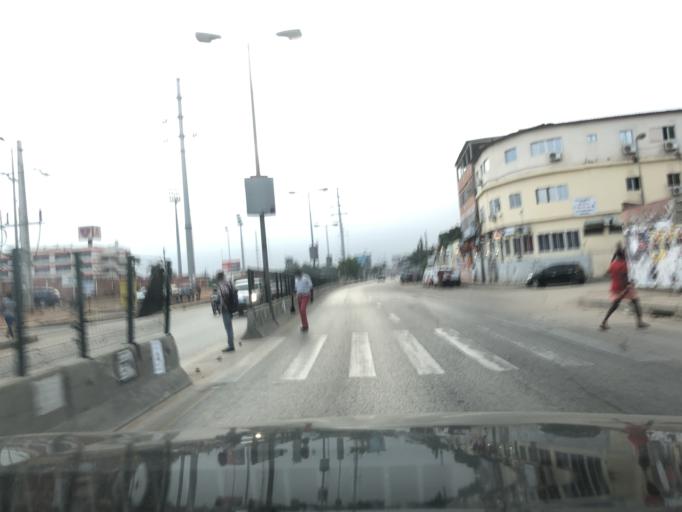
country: AO
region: Luanda
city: Luanda
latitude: -8.8436
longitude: 13.2395
